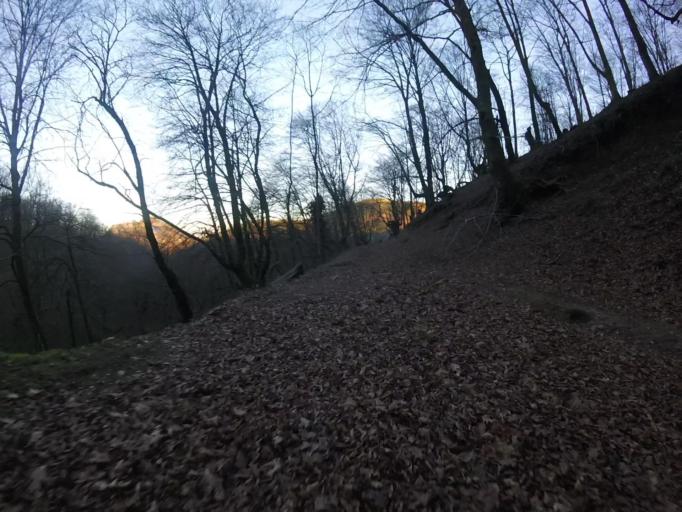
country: ES
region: Basque Country
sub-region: Provincia de Guipuzcoa
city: Irun
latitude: 43.2550
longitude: -1.8219
